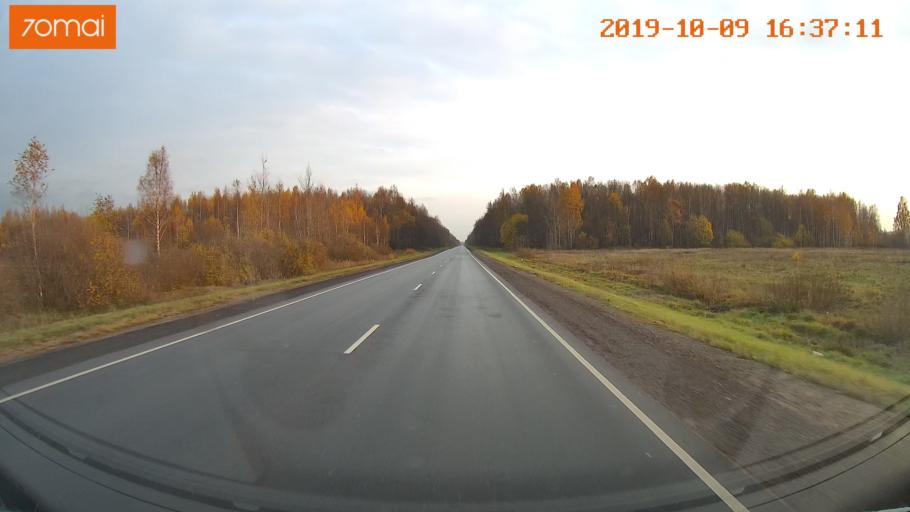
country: RU
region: Kostroma
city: Volgorechensk
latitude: 57.5308
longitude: 41.0215
